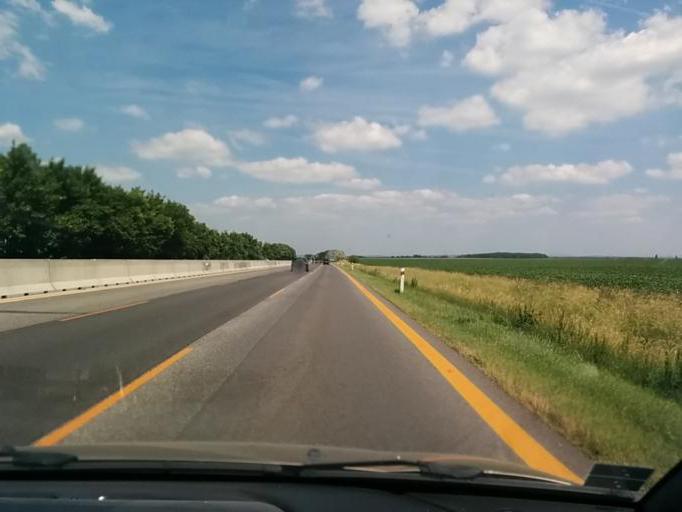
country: SK
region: Trnavsky
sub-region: Okres Trnava
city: Trnava
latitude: 48.3136
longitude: 17.5787
